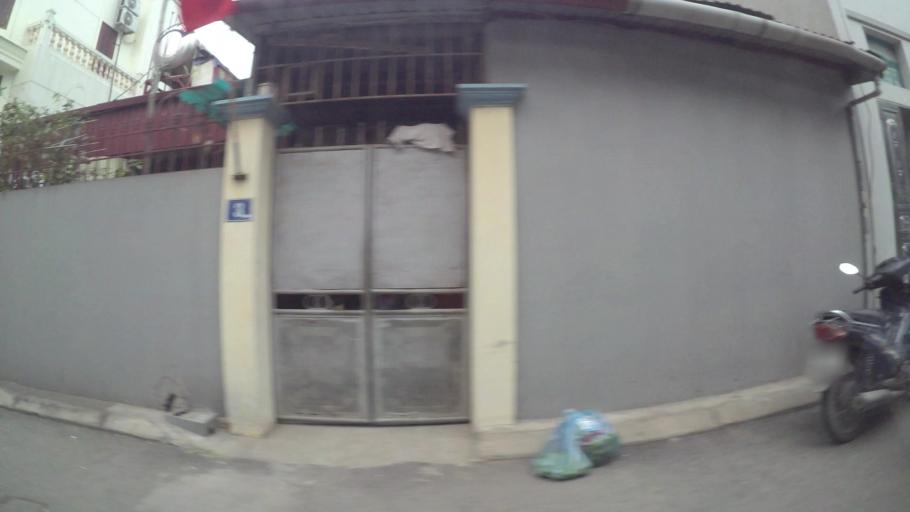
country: VN
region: Ha Noi
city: Trau Quy
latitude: 21.0564
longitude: 105.8984
